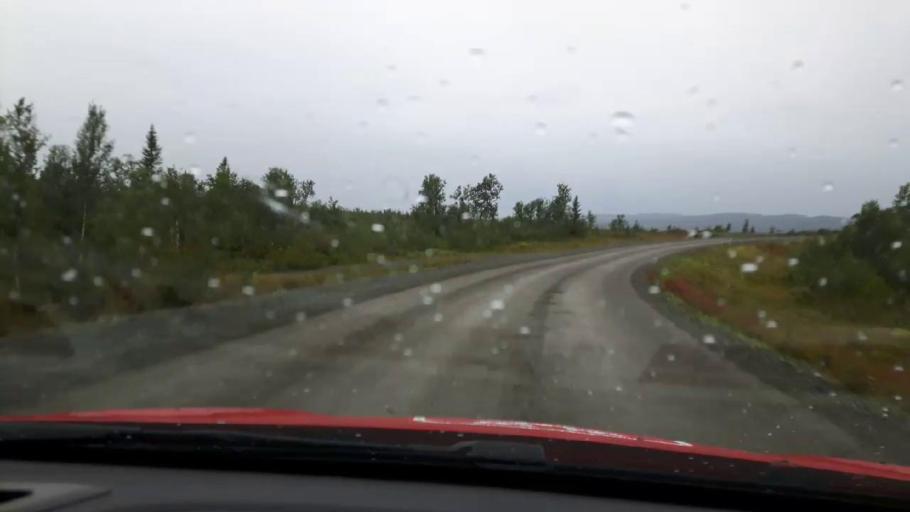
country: NO
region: Nord-Trondelag
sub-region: Meraker
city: Meraker
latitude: 63.5976
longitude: 12.2793
